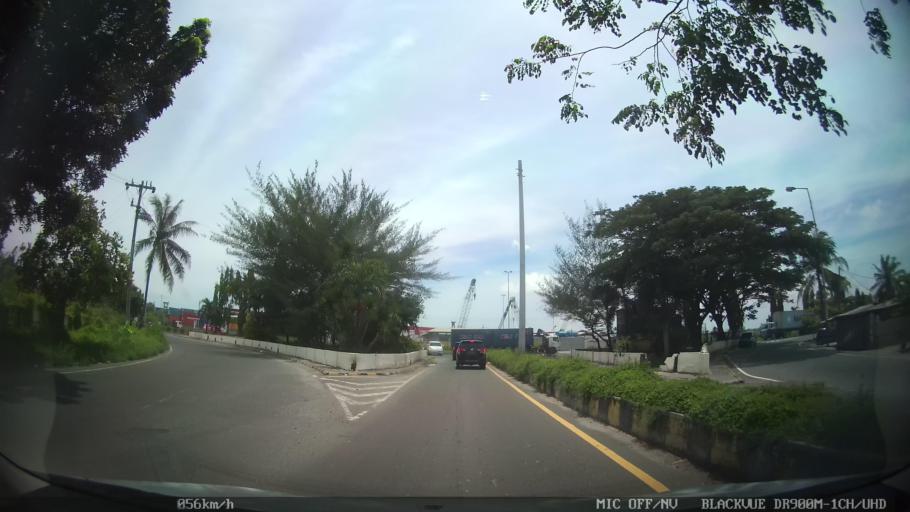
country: ID
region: North Sumatra
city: Belawan
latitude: 3.7721
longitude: 98.6838
